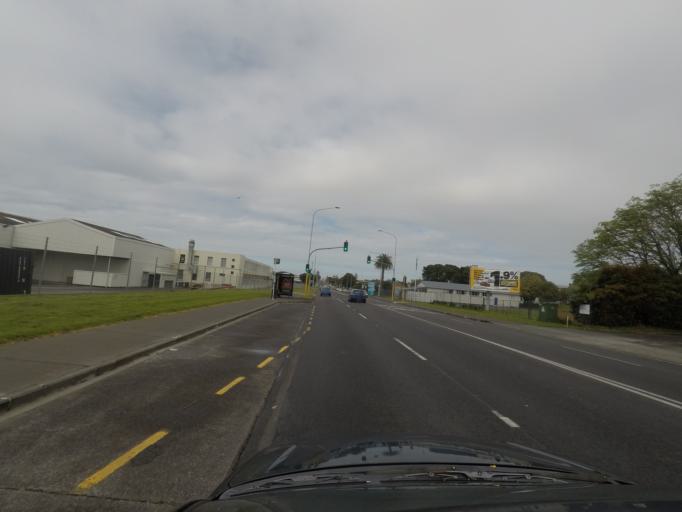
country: NZ
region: Auckland
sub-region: Auckland
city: Tamaki
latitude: -36.9008
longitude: 174.8436
